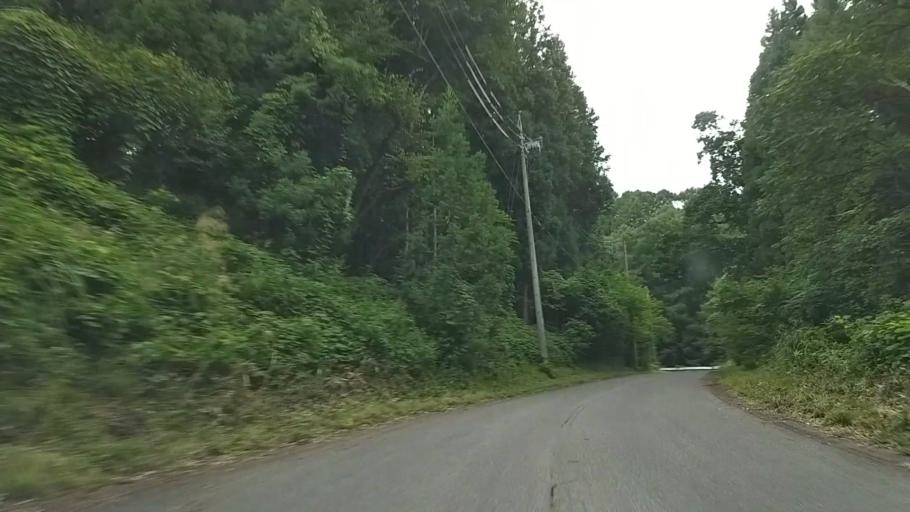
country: JP
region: Nagano
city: Iiyama
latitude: 36.8150
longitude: 138.3705
